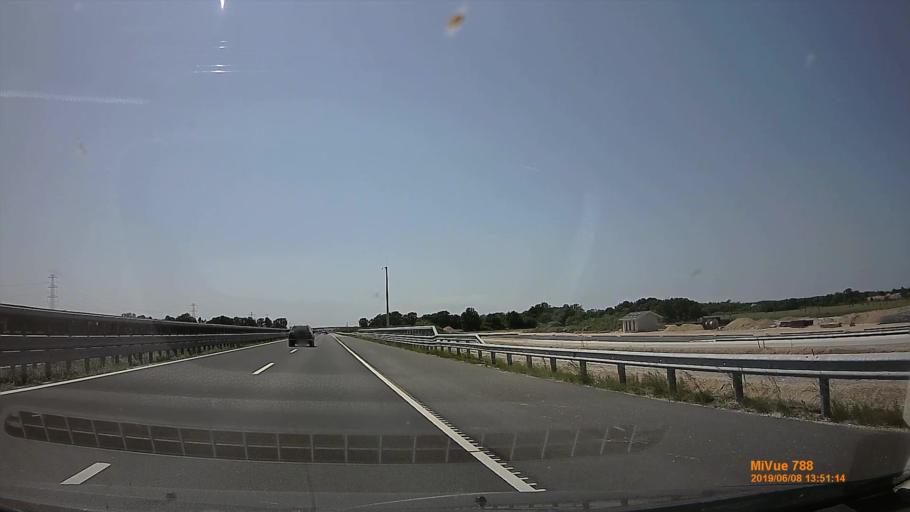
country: HU
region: Vas
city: Repcelak
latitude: 47.3848
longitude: 16.9743
